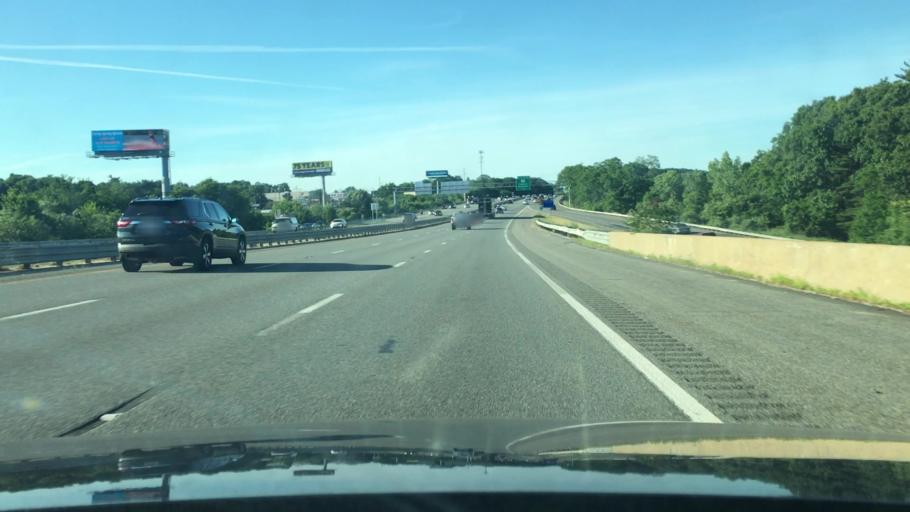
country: US
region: Massachusetts
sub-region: Essex County
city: South Peabody
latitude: 42.5429
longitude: -70.9837
